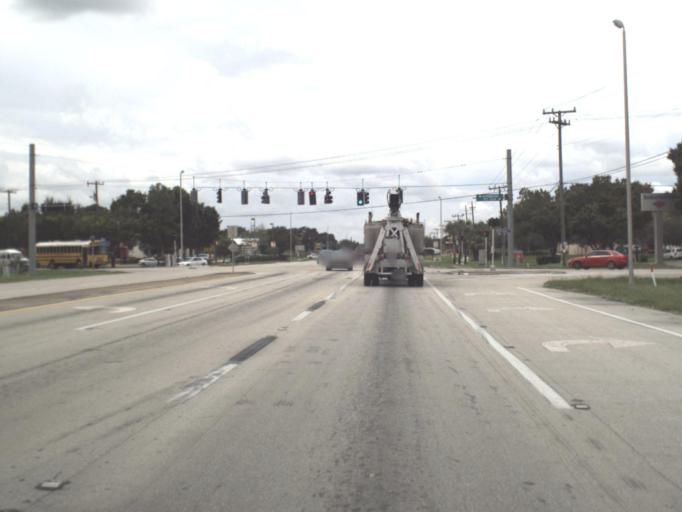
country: US
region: Florida
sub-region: Lee County
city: Olga
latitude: 26.7101
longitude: -81.7201
